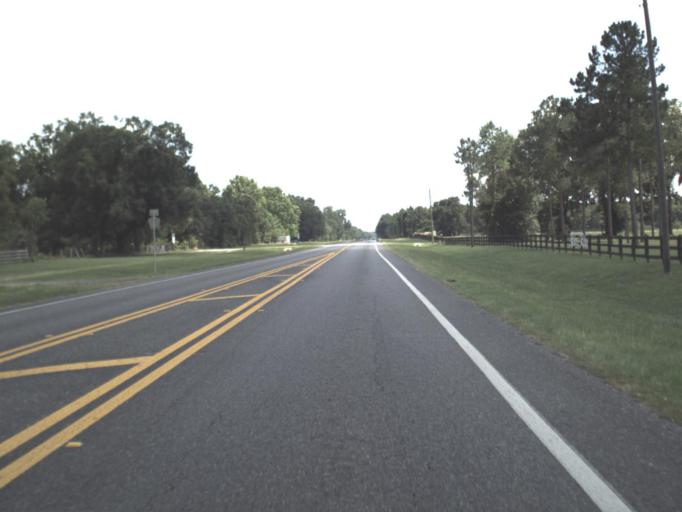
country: US
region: Florida
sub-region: Alachua County
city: High Springs
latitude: 29.8851
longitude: -82.6091
